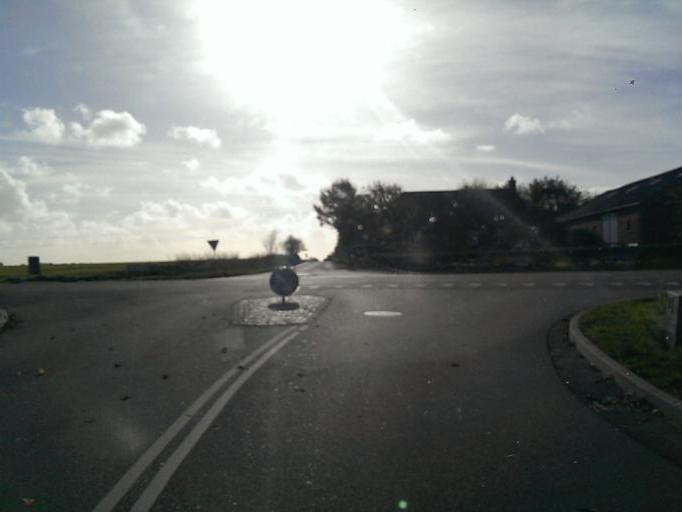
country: DK
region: South Denmark
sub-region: Esbjerg Kommune
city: Tjaereborg
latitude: 55.4592
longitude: 8.5729
